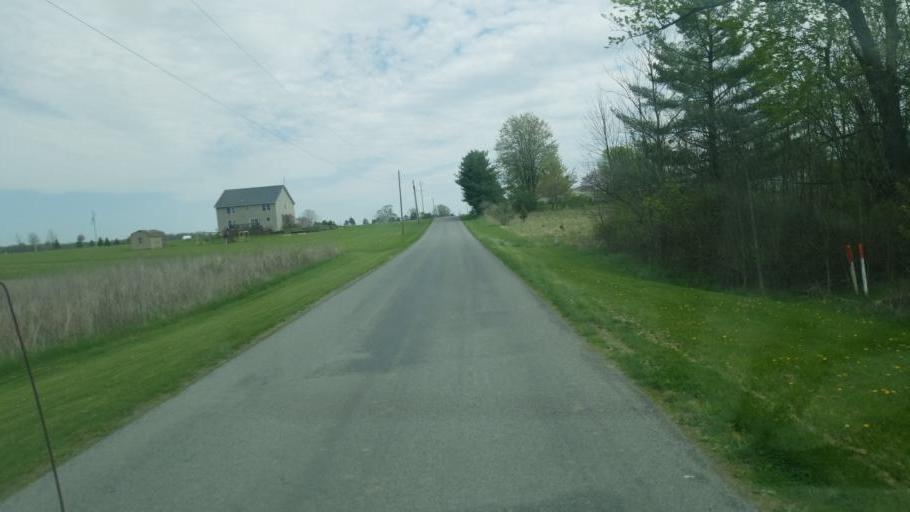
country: US
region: Ohio
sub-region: Allen County
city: Bluffton
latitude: 40.8117
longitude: -83.9541
